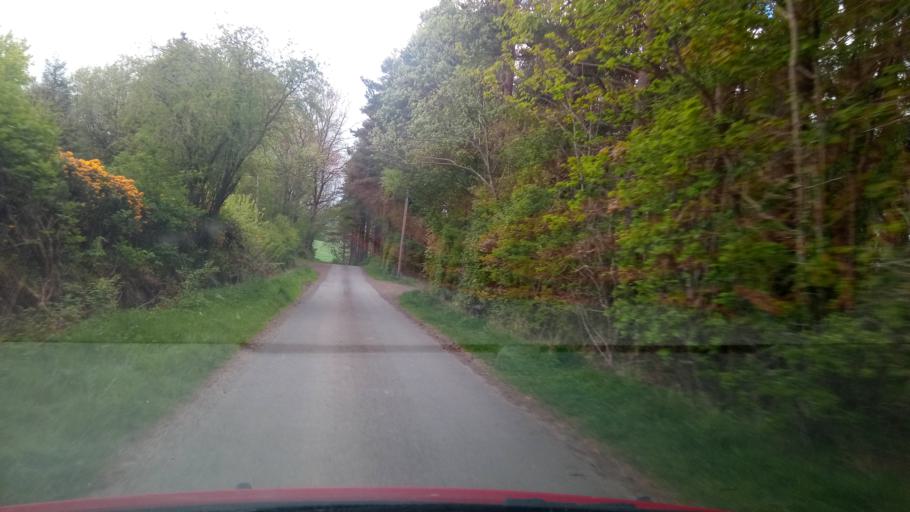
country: GB
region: Scotland
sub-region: The Scottish Borders
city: Saint Boswells
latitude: 55.5088
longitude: -2.6554
